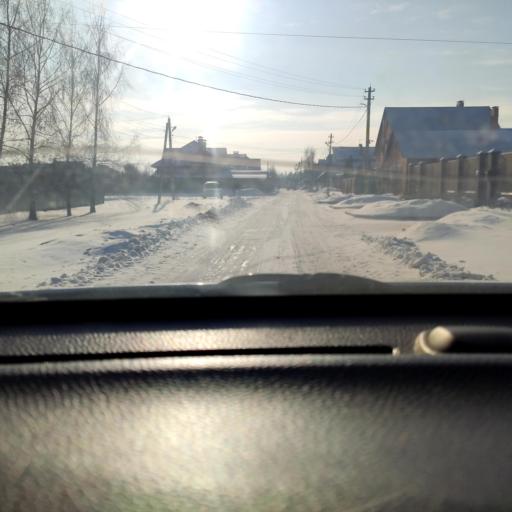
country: RU
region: Voronezj
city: Somovo
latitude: 51.6822
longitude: 39.3176
